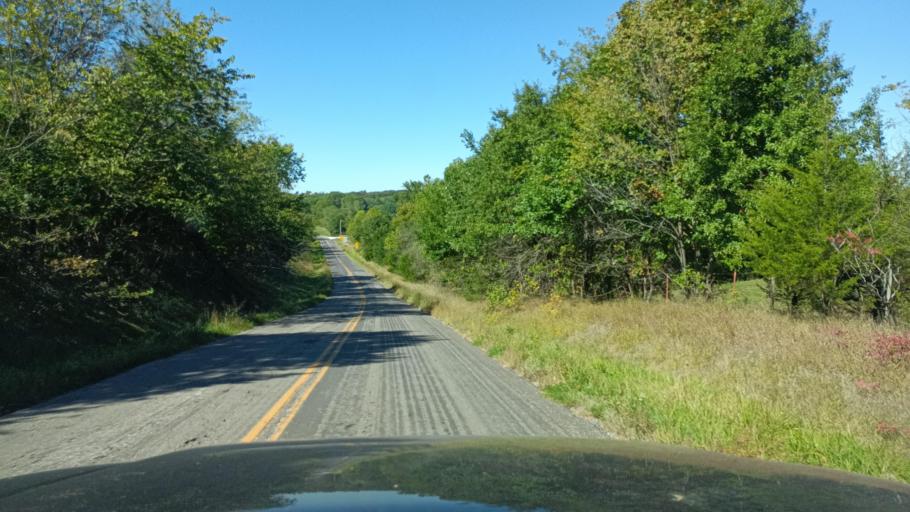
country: US
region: Missouri
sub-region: Scotland County
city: Memphis
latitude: 40.3501
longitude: -92.3175
